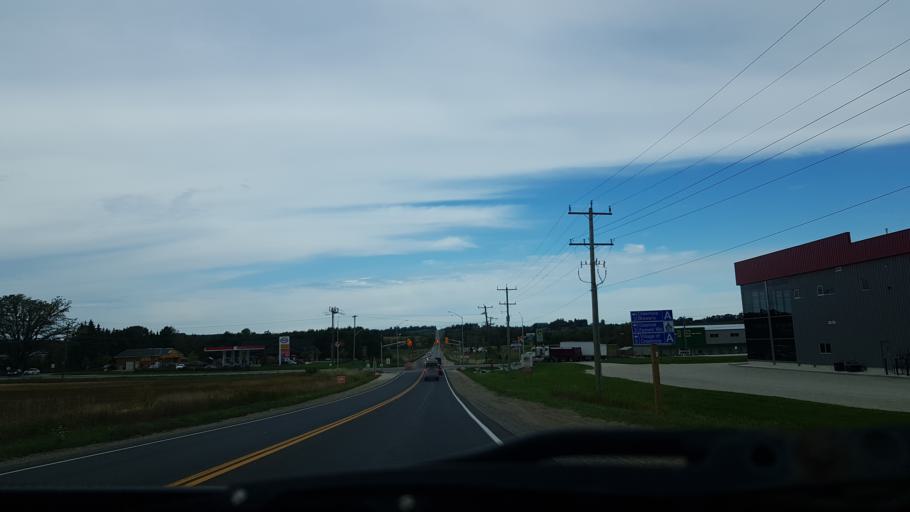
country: CA
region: Ontario
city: Wasaga Beach
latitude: 44.3352
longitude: -80.0779
